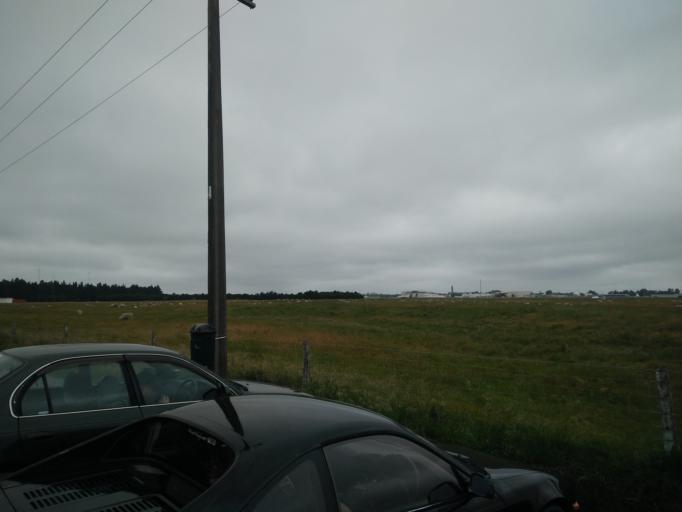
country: NZ
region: Canterbury
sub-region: Selwyn District
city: Prebbleton
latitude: -43.4797
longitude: 172.5308
